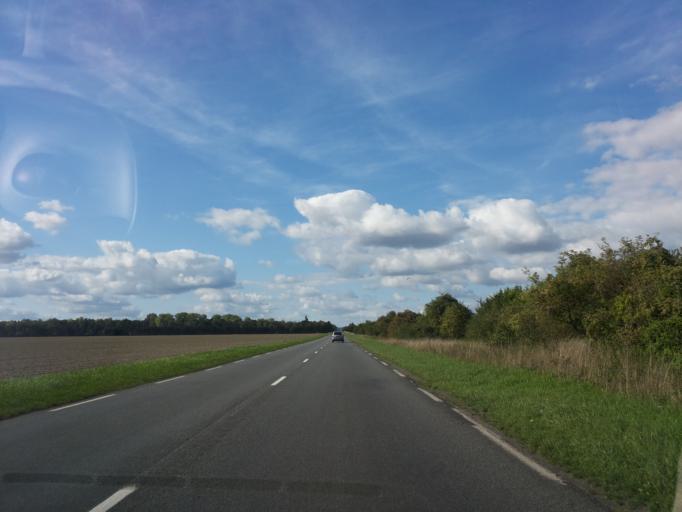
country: FR
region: Champagne-Ardenne
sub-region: Departement de la Marne
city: Cormicy
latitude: 49.4174
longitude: 3.8808
